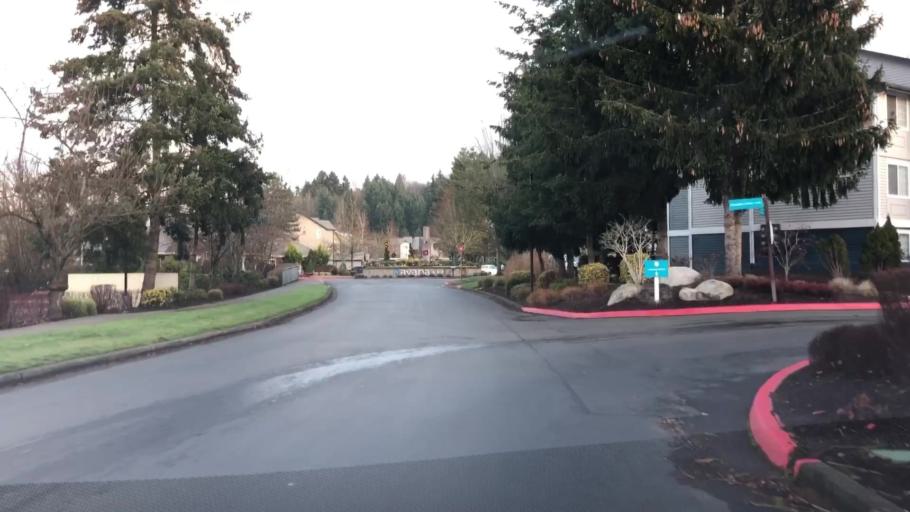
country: US
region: Washington
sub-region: King County
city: Woodinville
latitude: 47.7590
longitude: -122.1725
